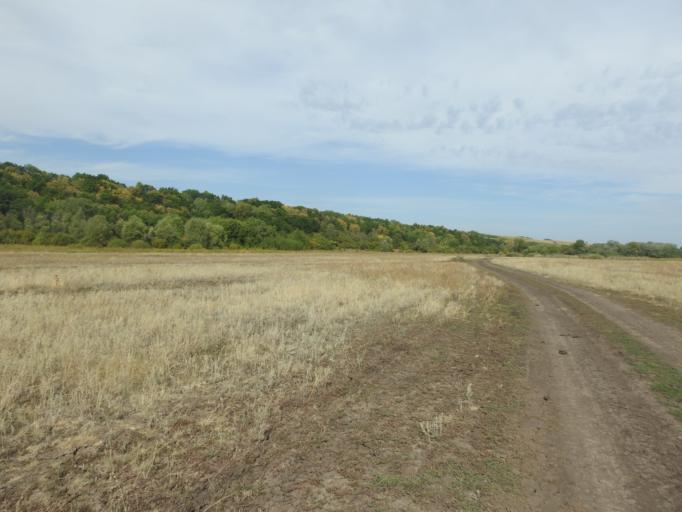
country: RU
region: Volgograd
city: Zhirnovsk
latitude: 51.1941
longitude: 44.9469
